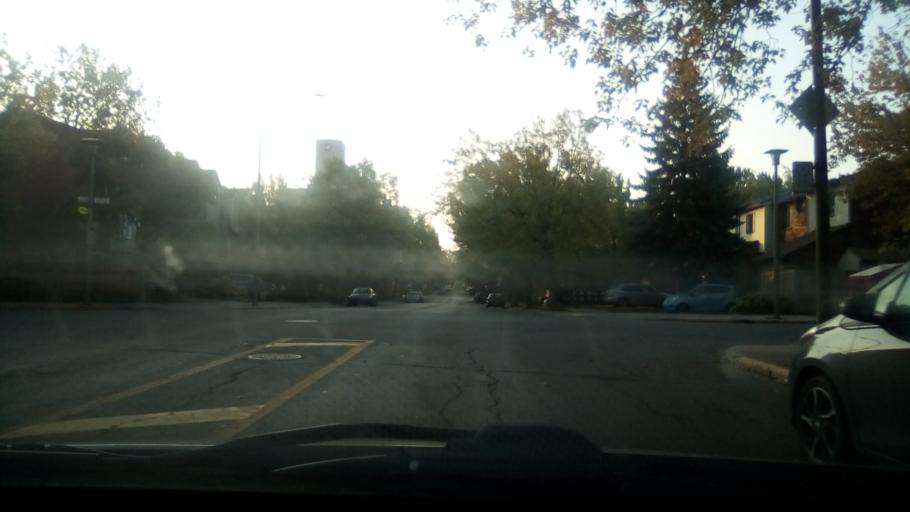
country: CA
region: Quebec
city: Westmount
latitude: 45.4862
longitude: -73.5732
